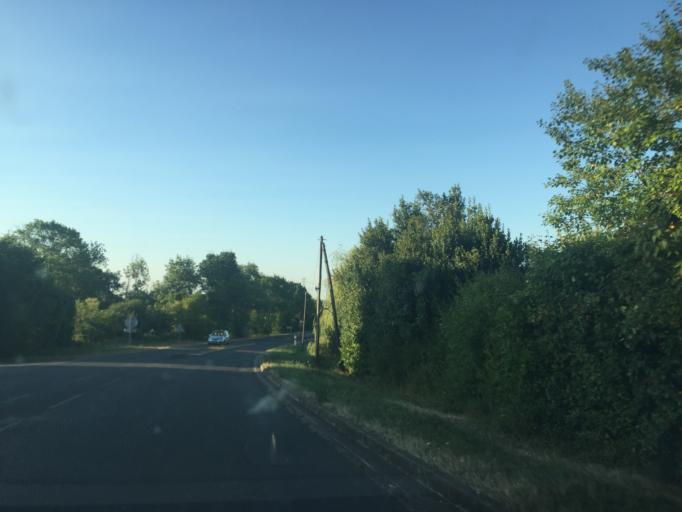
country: FR
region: Poitou-Charentes
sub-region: Departement des Deux-Sevres
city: Lezay
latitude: 46.3051
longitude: -0.0507
